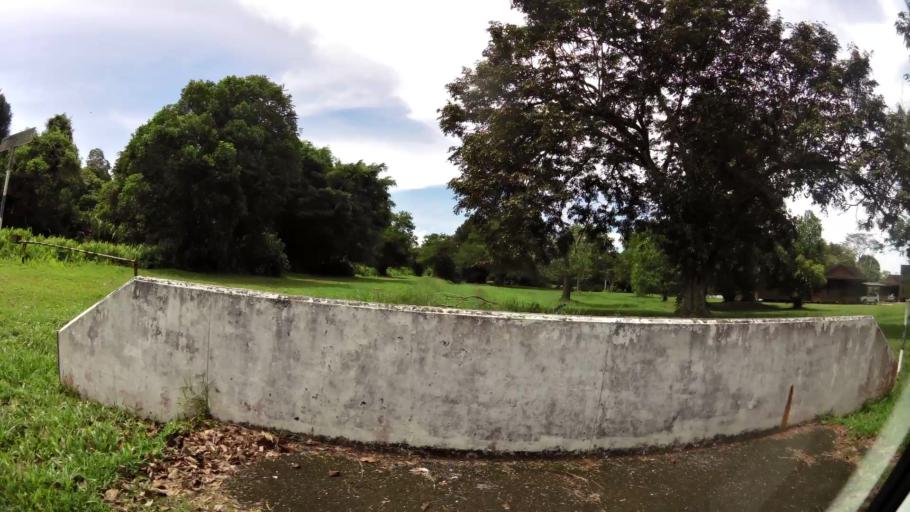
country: BN
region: Belait
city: Seria
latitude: 4.5929
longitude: 114.2842
